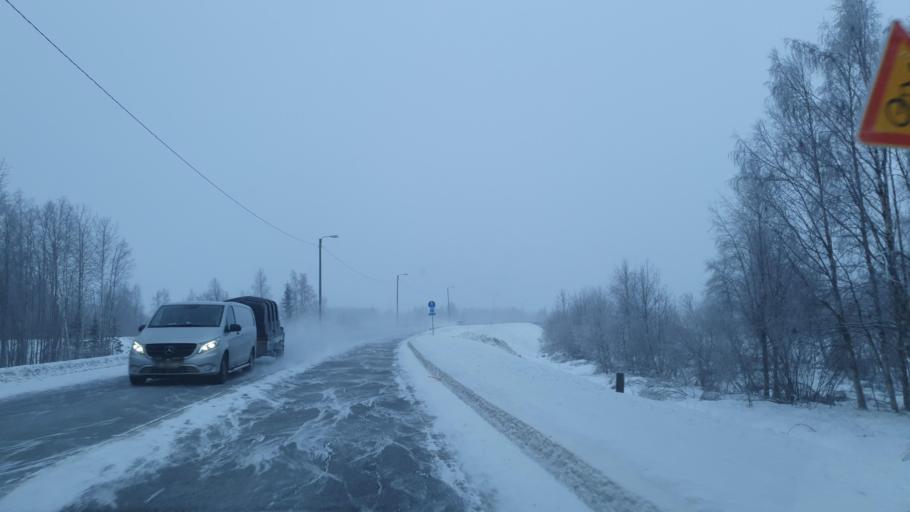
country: FI
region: Lapland
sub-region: Kemi-Tornio
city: Tornio
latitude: 66.0143
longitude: 24.0659
